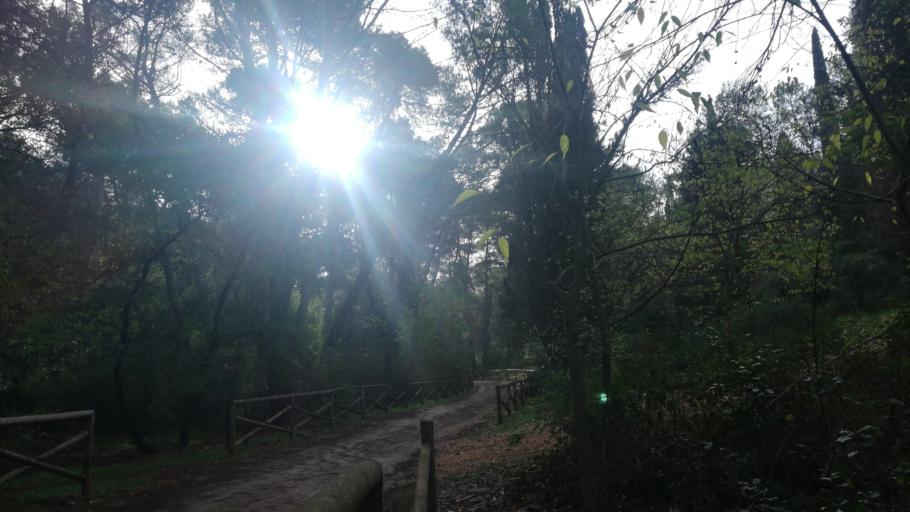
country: IT
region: Apulia
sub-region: Provincia di Bari
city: Cassano delle Murge
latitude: 40.8859
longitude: 16.7022
